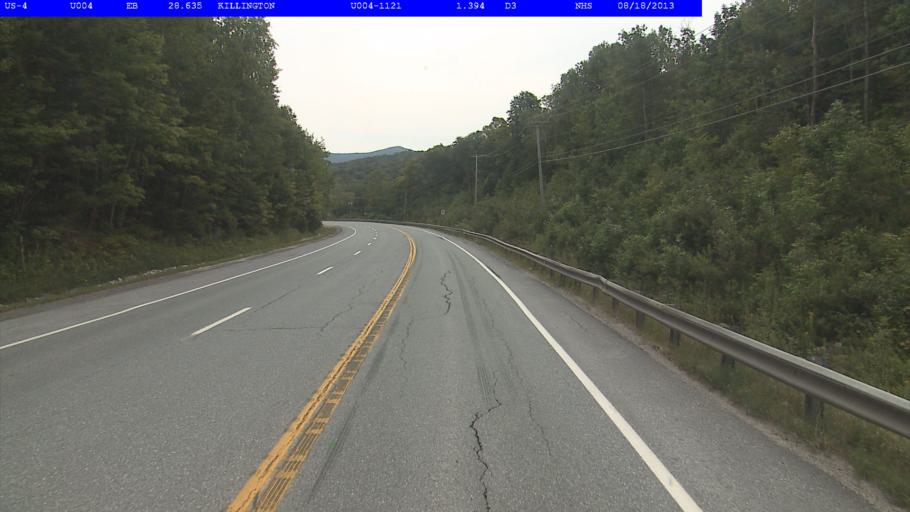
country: US
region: Vermont
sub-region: Rutland County
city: Rutland
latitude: 43.6631
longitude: -72.8198
